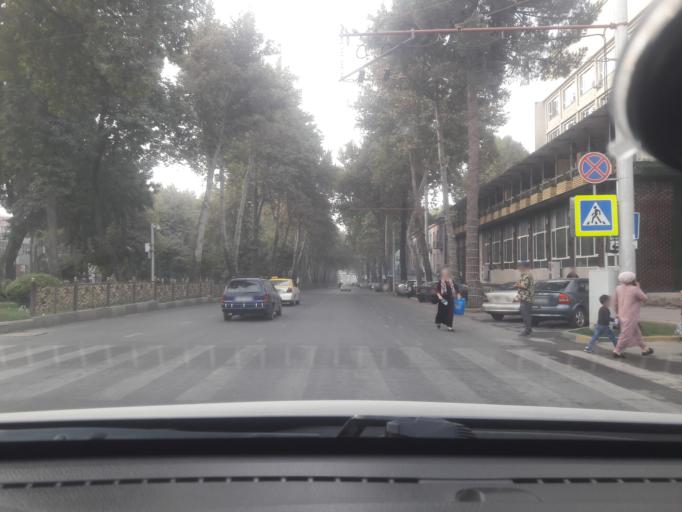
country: TJ
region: Dushanbe
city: Dushanbe
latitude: 38.5622
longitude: 68.7989
